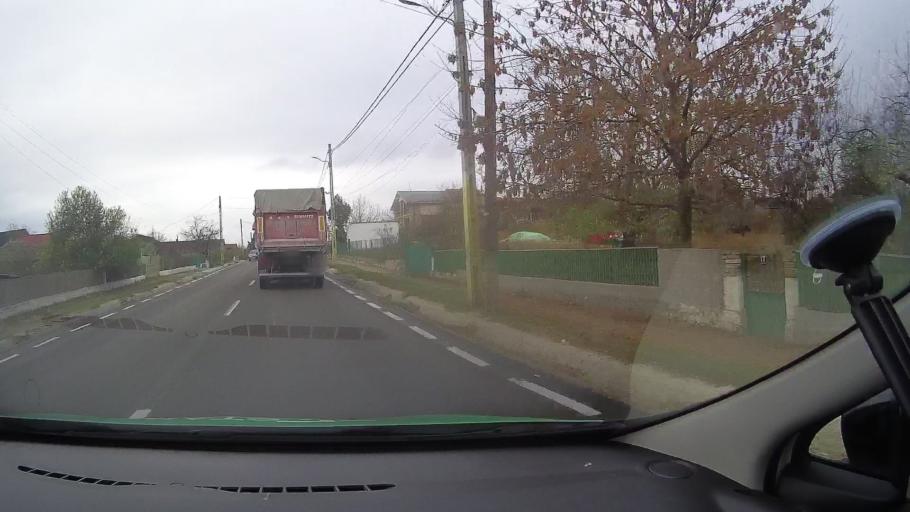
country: RO
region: Constanta
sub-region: Comuna Poarta Alba
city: Poarta Alba
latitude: 44.2095
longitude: 28.3947
